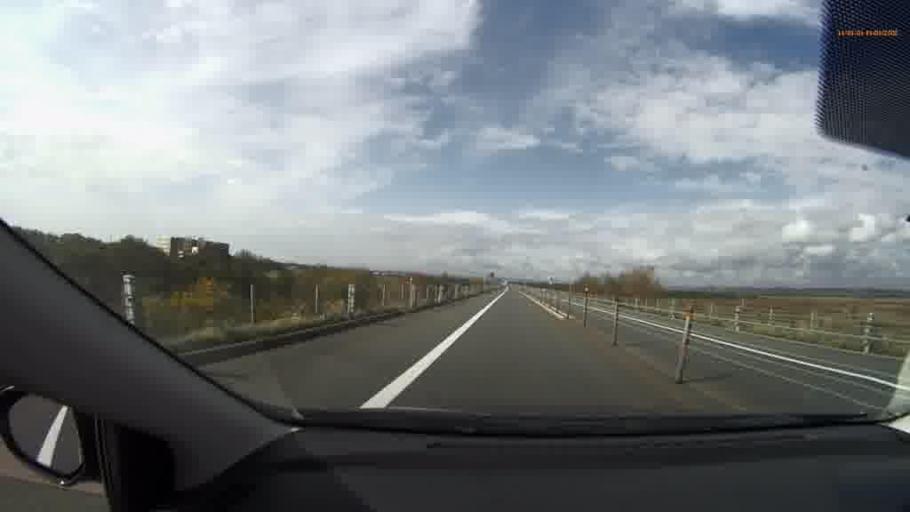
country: JP
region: Hokkaido
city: Kushiro
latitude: 43.0362
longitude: 144.3607
